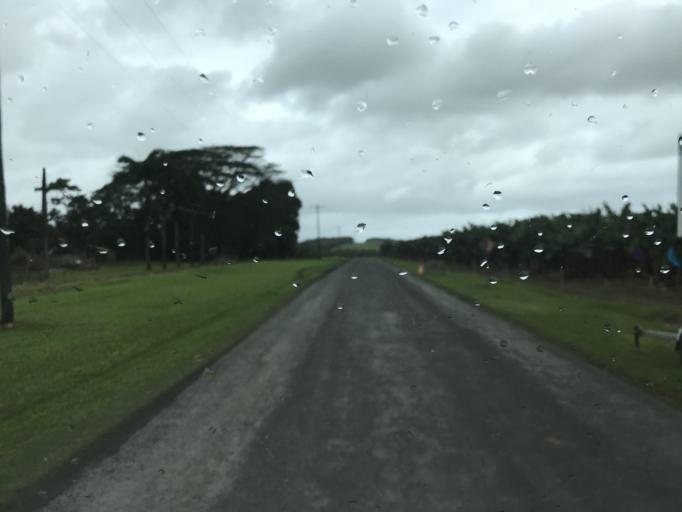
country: AU
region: Queensland
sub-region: Cassowary Coast
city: Innisfail
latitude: -17.5026
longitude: 145.9815
